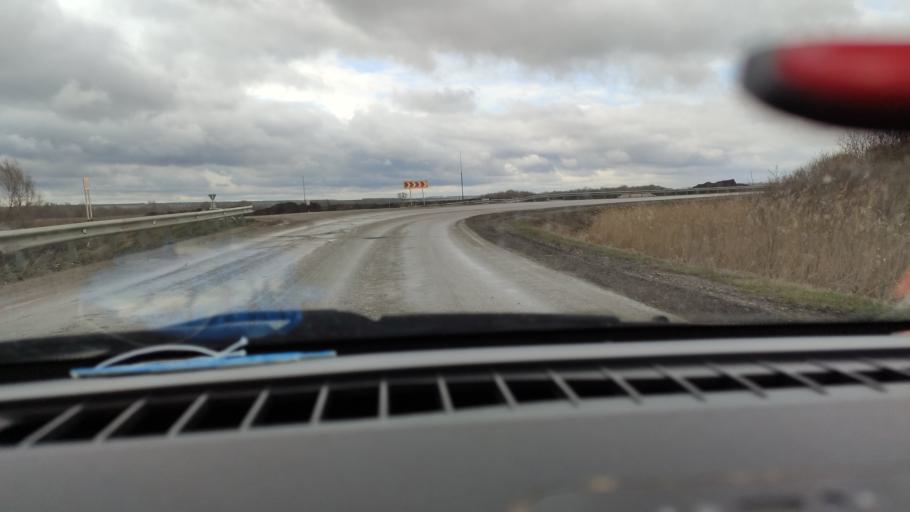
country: RU
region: Tatarstan
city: Nurlat
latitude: 54.3678
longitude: 50.7110
